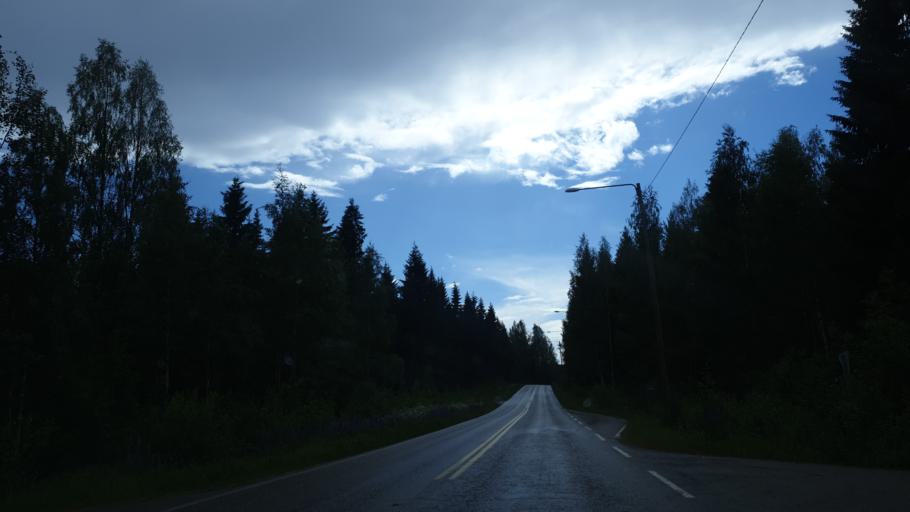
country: FI
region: Northern Savo
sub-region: Kuopio
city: Kuopio
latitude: 62.9107
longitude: 27.8668
